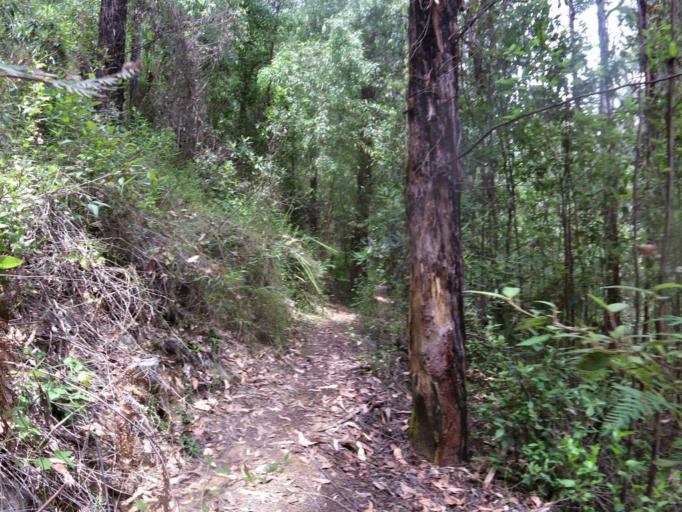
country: AU
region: Victoria
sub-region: Yarra Ranges
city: Healesville
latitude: -37.4558
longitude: 145.5738
